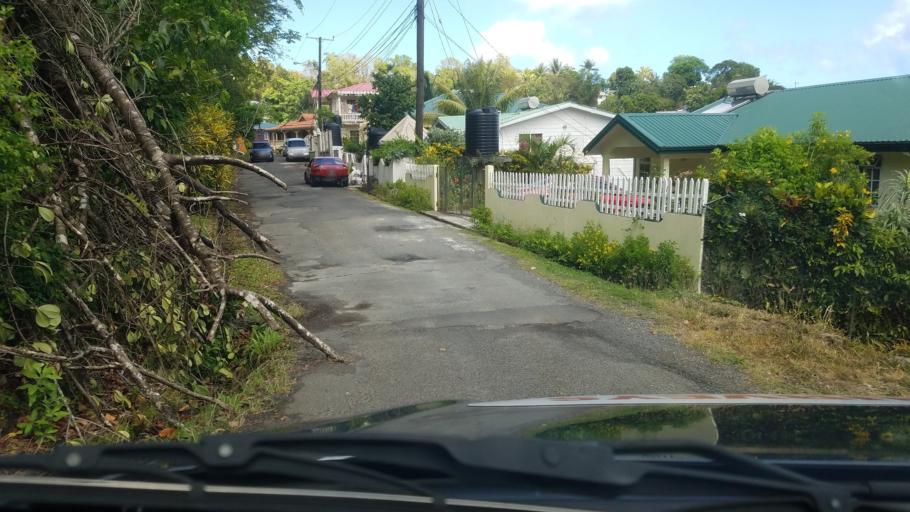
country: LC
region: Castries Quarter
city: Bisee
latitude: 14.0160
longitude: -60.9814
